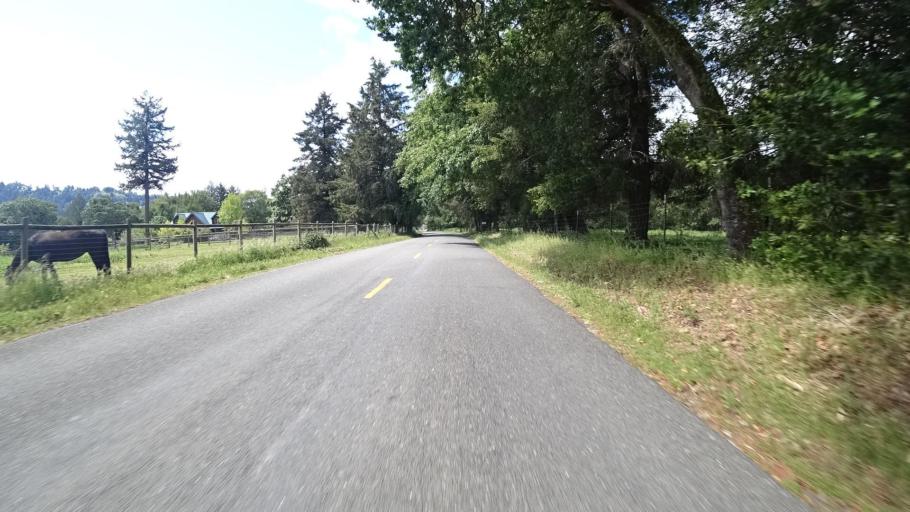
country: US
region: California
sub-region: Humboldt County
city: Redway
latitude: 40.0896
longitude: -123.8085
